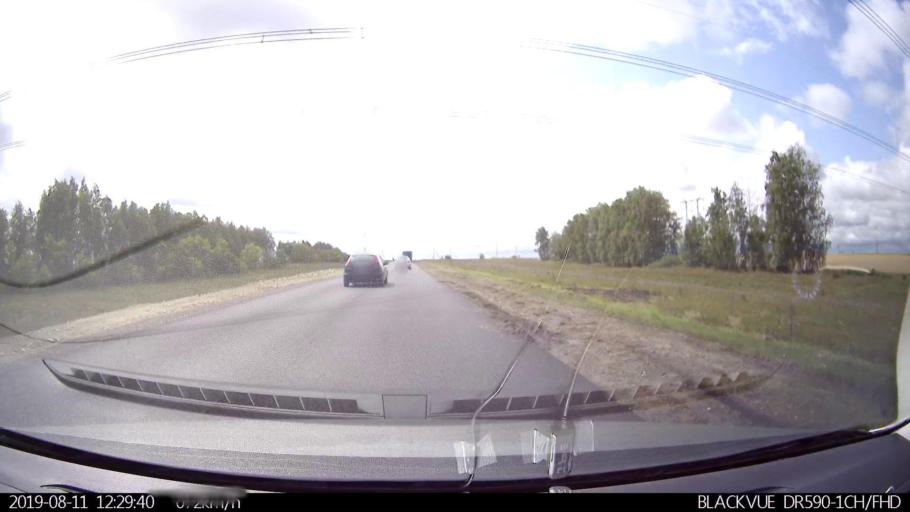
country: RU
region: Ulyanovsk
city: Ignatovka
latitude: 53.8326
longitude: 47.9007
